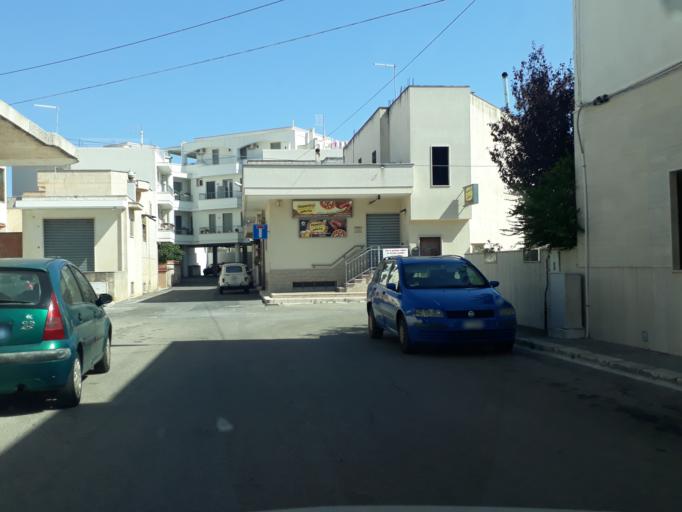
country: IT
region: Apulia
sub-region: Provincia di Brindisi
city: Carovigno
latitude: 40.7131
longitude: 17.6566
